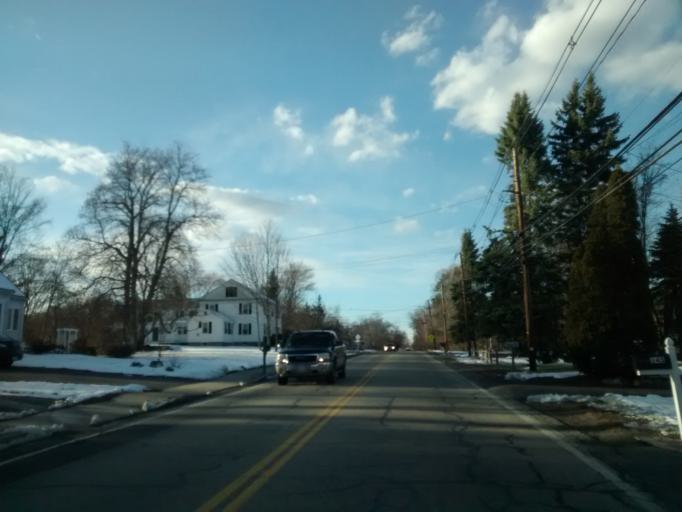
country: US
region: Massachusetts
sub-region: Middlesex County
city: Hopkinton
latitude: 42.2113
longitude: -71.5138
